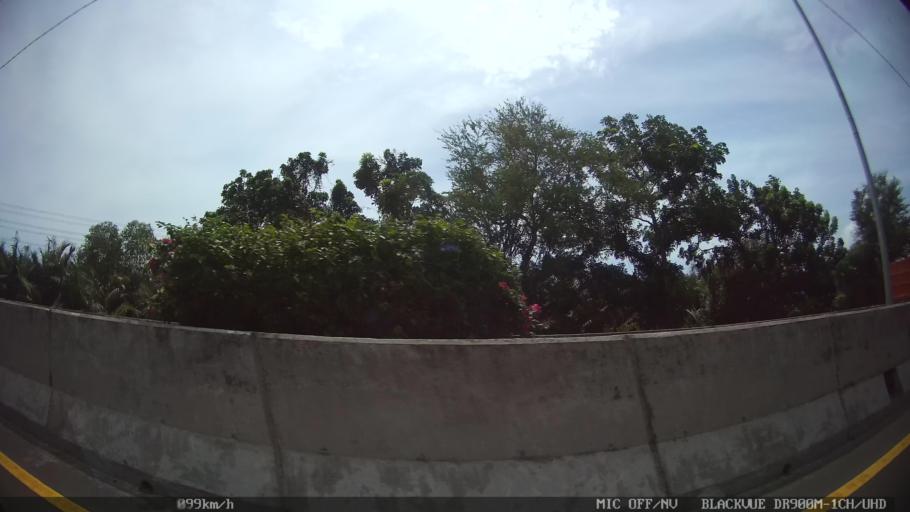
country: ID
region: North Sumatra
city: Labuhan Deli
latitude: 3.7454
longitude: 98.6799
